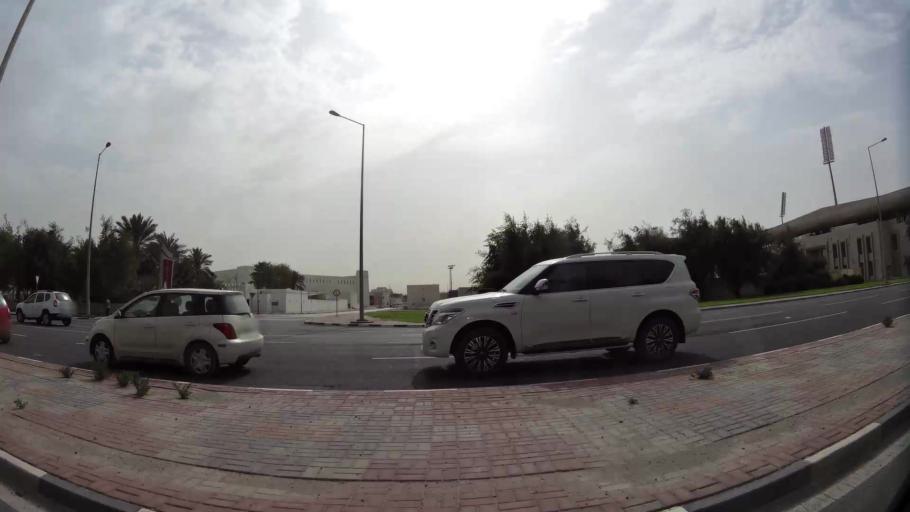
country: QA
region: Baladiyat ad Dawhah
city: Doha
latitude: 25.3160
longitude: 51.5149
